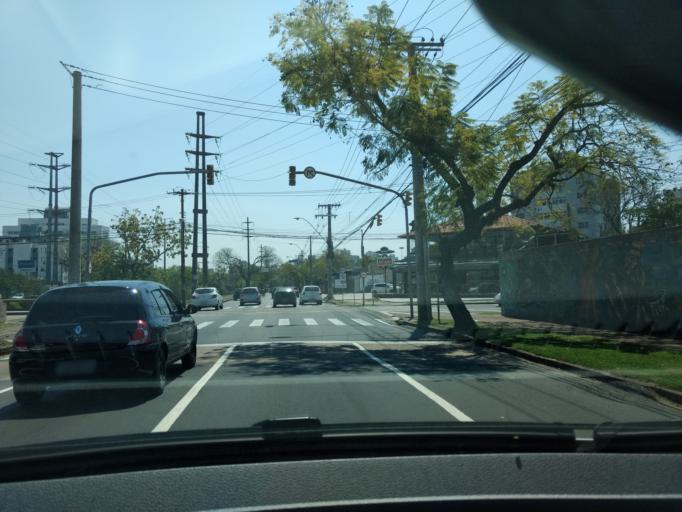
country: BR
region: Rio Grande do Sul
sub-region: Porto Alegre
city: Porto Alegre
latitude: -30.0467
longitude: -51.1975
